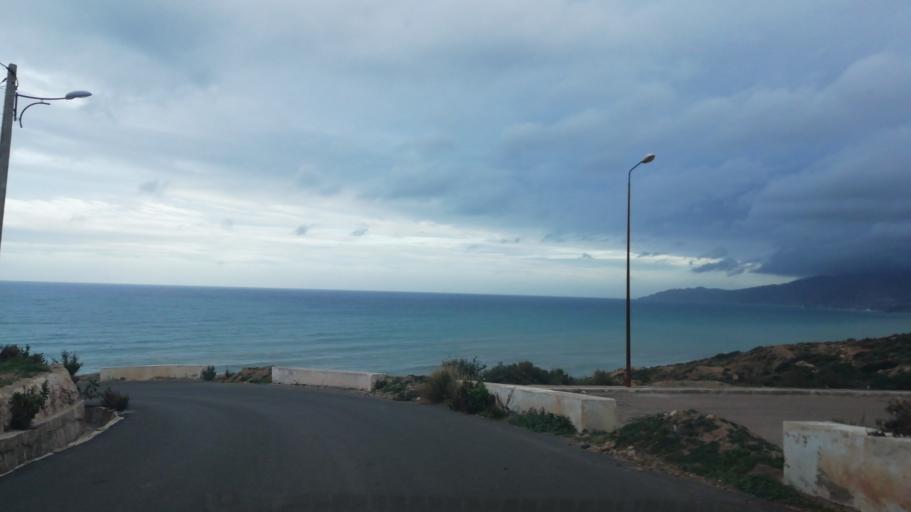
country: DZ
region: Oran
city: Bir el Djir
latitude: 35.7680
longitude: -0.5268
